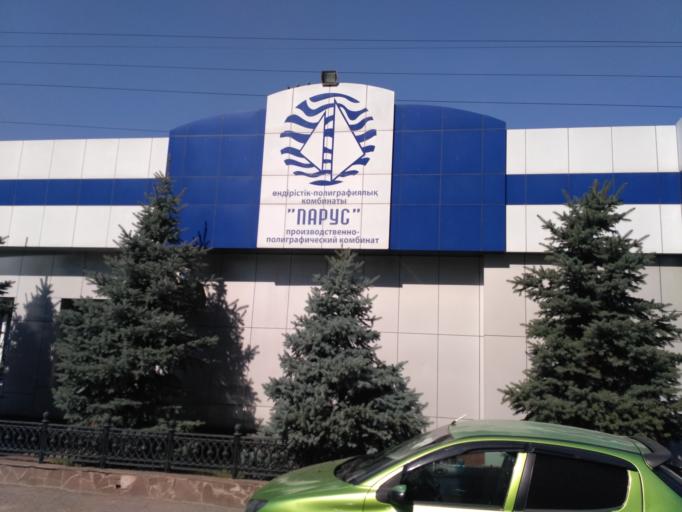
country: KZ
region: Almaty Qalasy
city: Almaty
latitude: 43.2441
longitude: 76.8520
